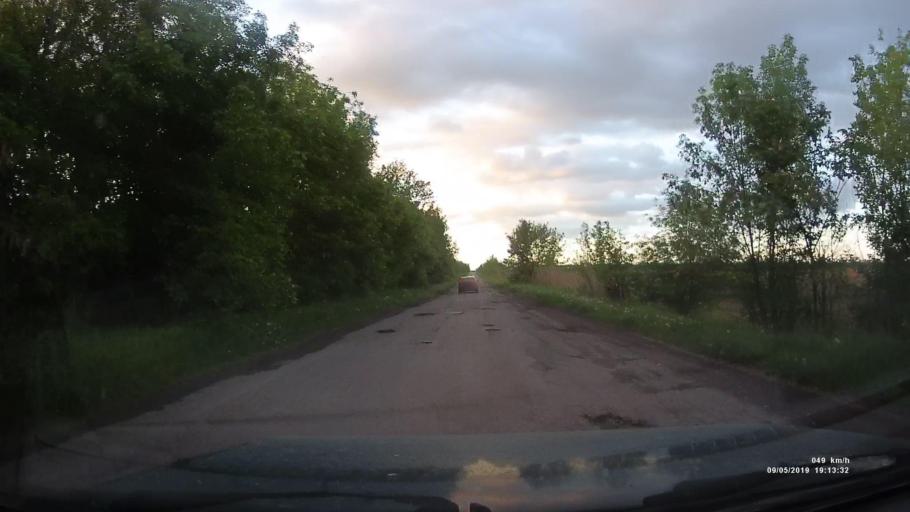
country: RU
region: Krasnodarskiy
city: Kanelovskaya
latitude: 46.7514
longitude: 39.2138
